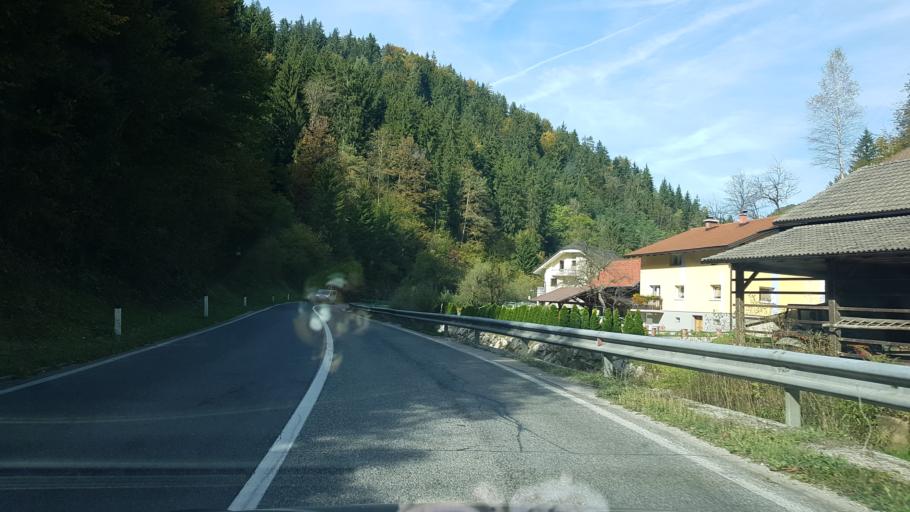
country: SI
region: Dobrna
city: Dobrna
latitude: 46.4038
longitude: 15.1797
